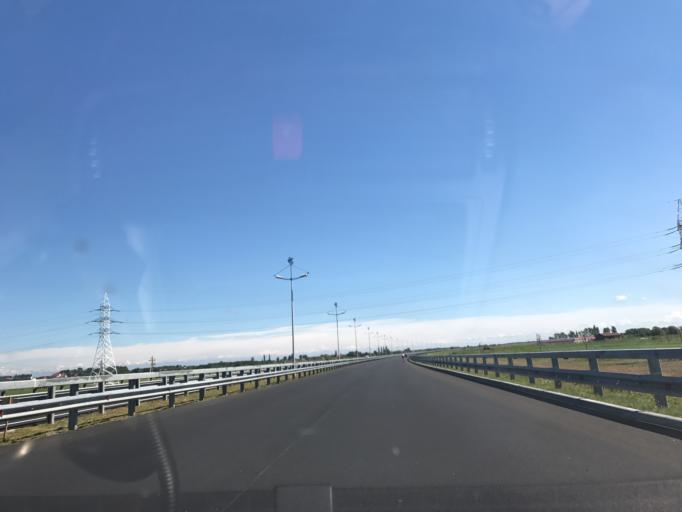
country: RU
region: Kaliningrad
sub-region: Zelenogradskiy Rayon
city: Zelenogradsk
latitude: 54.9202
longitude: 20.4527
